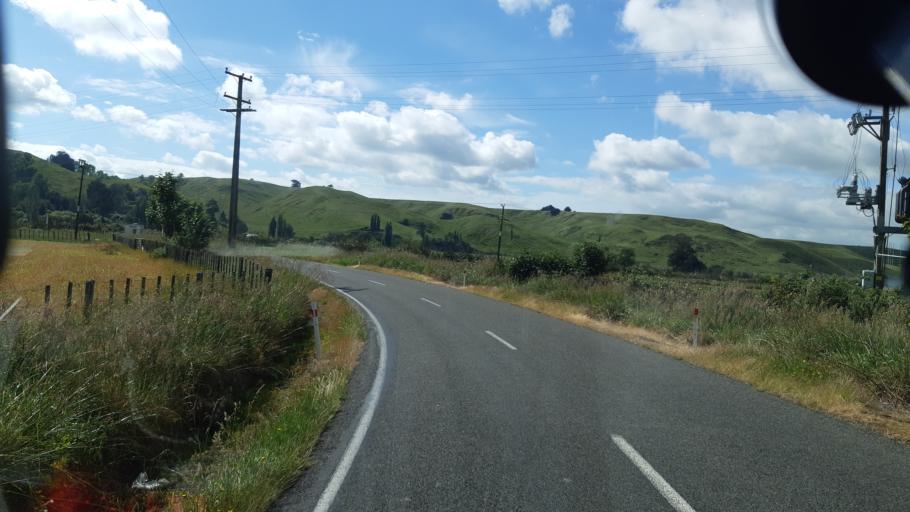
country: NZ
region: Manawatu-Wanganui
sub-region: Rangitikei District
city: Bulls
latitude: -39.9678
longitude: 175.5202
